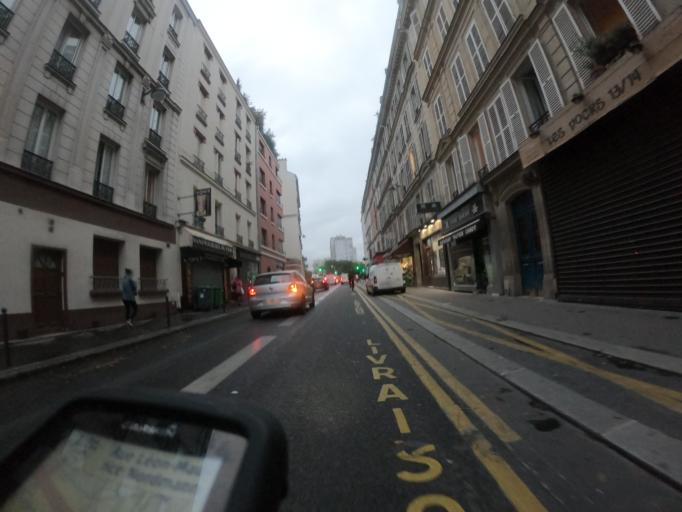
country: FR
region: Ile-de-France
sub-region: Departement du Val-de-Marne
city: Gentilly
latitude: 48.8254
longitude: 2.3417
